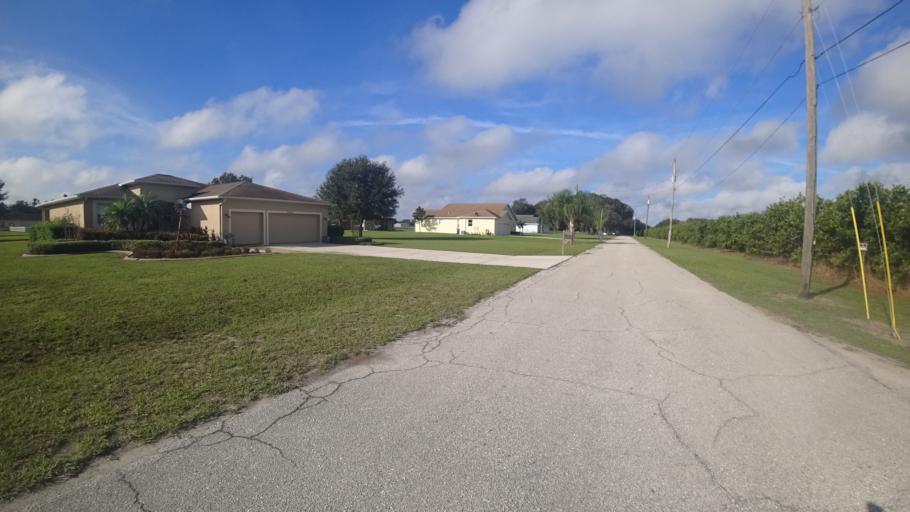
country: US
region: Florida
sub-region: Manatee County
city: Ellenton
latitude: 27.5722
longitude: -82.4050
